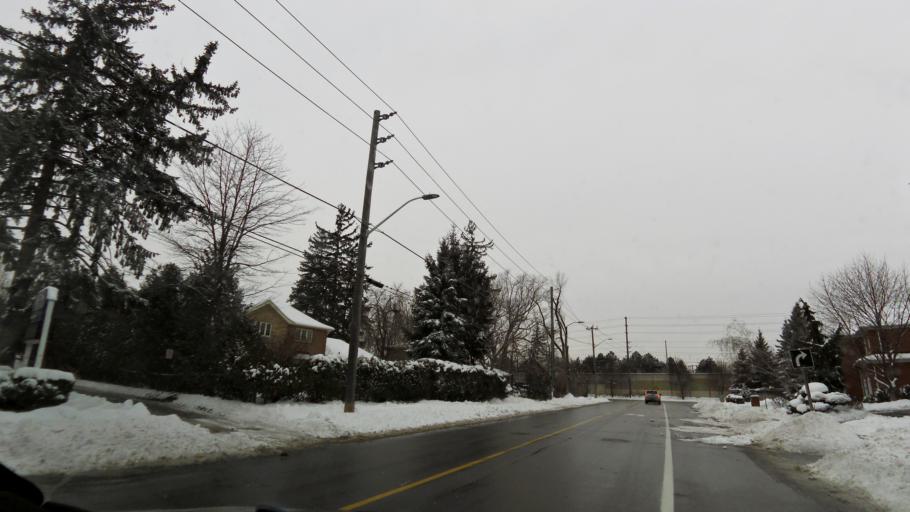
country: CA
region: Ontario
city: Mississauga
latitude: 43.5357
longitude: -79.6333
